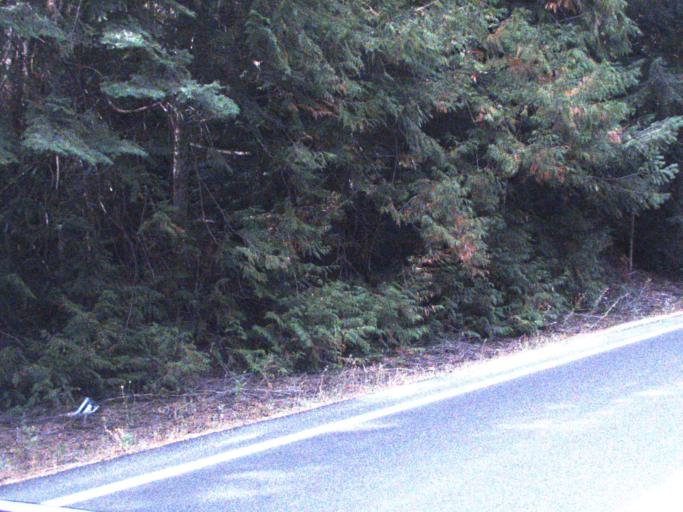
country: US
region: Washington
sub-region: Spokane County
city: Otis Orchards-East Farms
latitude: 47.8719
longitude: -117.1554
